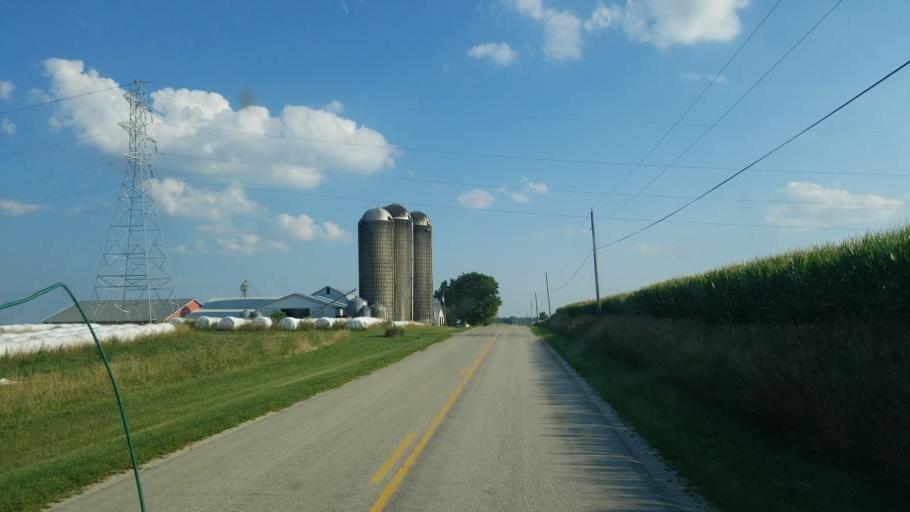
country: US
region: Ohio
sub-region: Crawford County
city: Bucyrus
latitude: 40.8545
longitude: -82.9018
